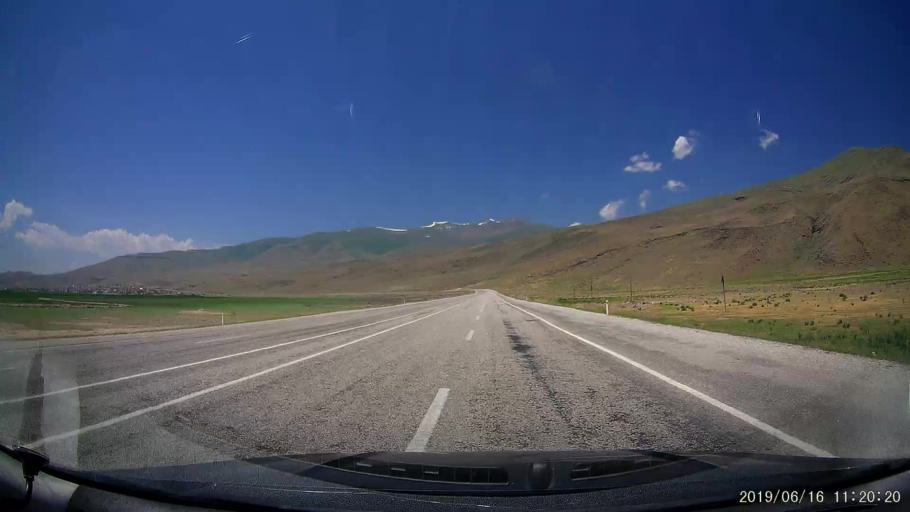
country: TR
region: Agri
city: Dogubayazit
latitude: 39.6984
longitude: 44.0929
